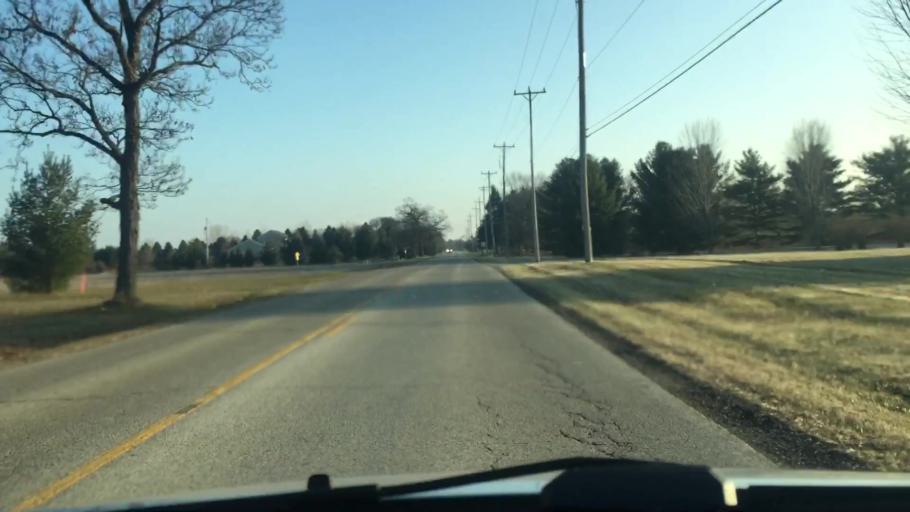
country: US
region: Wisconsin
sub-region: Waukesha County
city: Dousman
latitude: 43.0418
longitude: -88.4861
